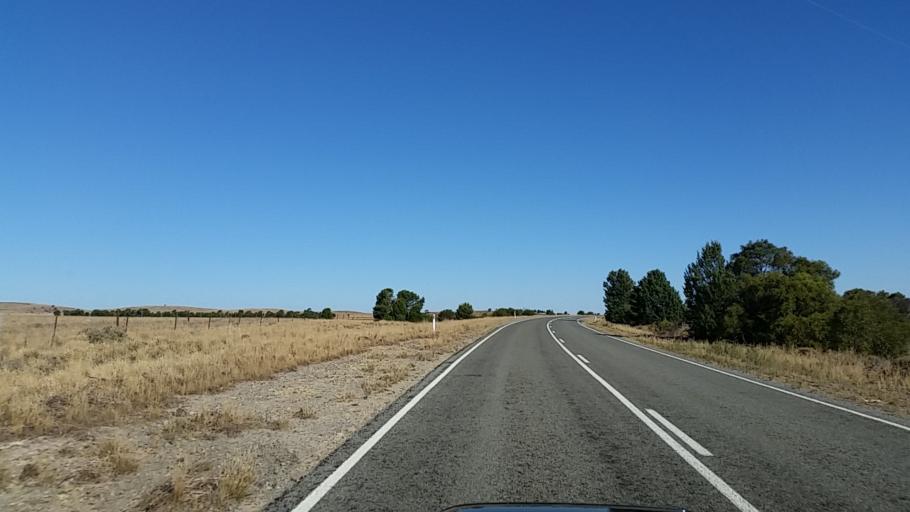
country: AU
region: South Australia
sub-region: Peterborough
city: Peterborough
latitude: -32.5426
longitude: 138.5596
